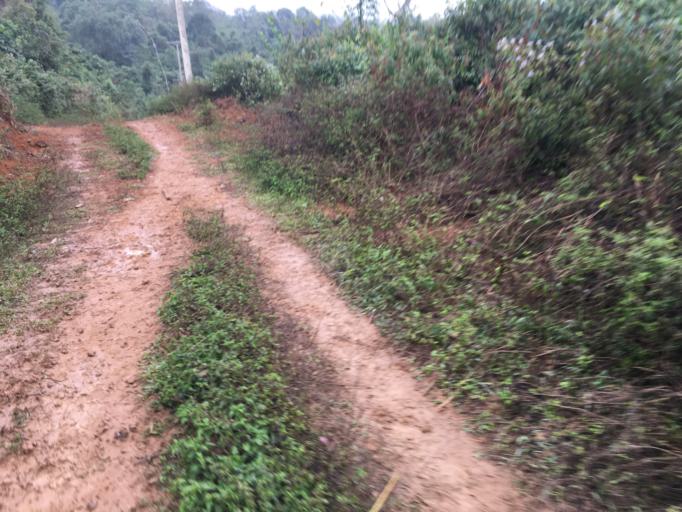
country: LA
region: Houaphan
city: Xamtay
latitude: 19.8962
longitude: 104.4618
